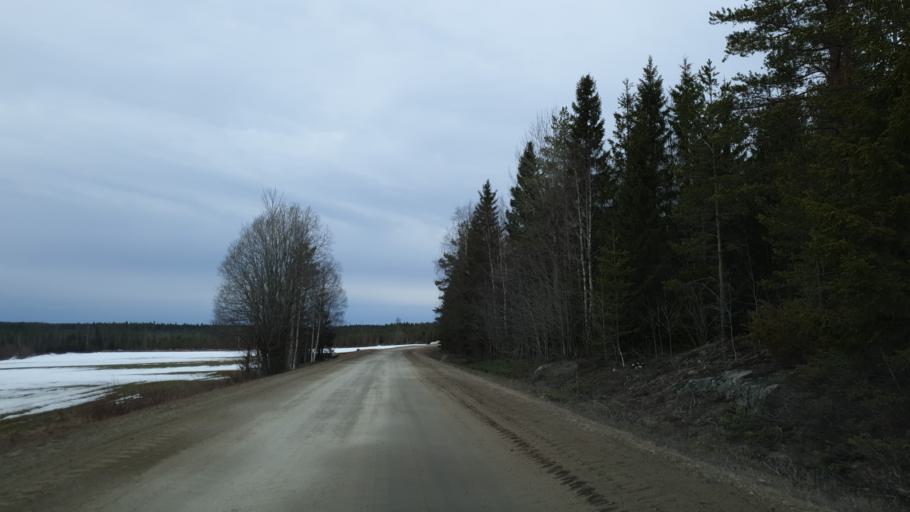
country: SE
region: Vaesterbotten
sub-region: Skelleftea Kommun
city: Burea
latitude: 64.3432
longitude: 21.1225
